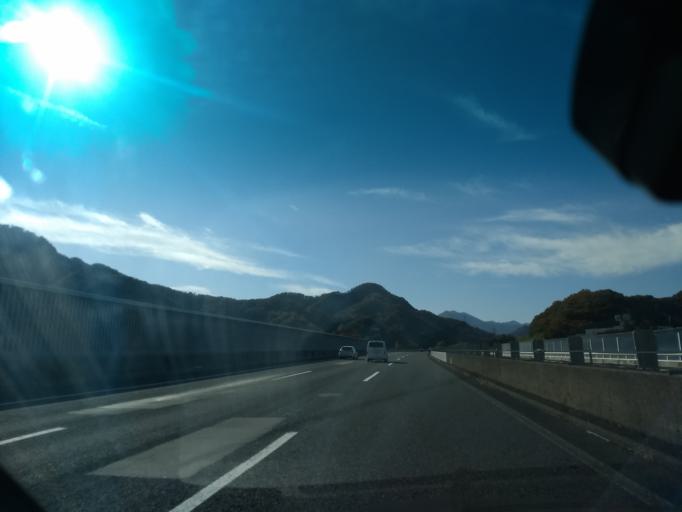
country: JP
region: Yamanashi
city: Otsuki
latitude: 35.6166
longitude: 138.9696
